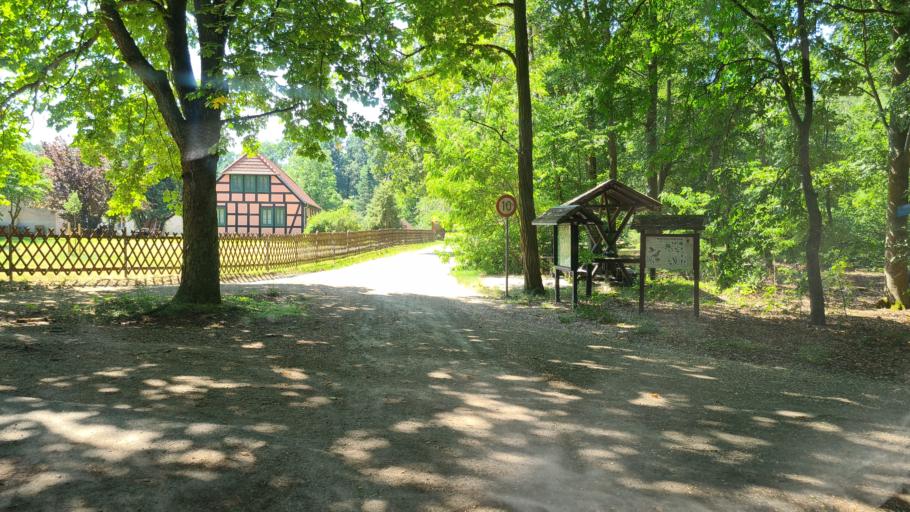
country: DE
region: Brandenburg
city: Lebusa
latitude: 51.7743
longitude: 13.4128
